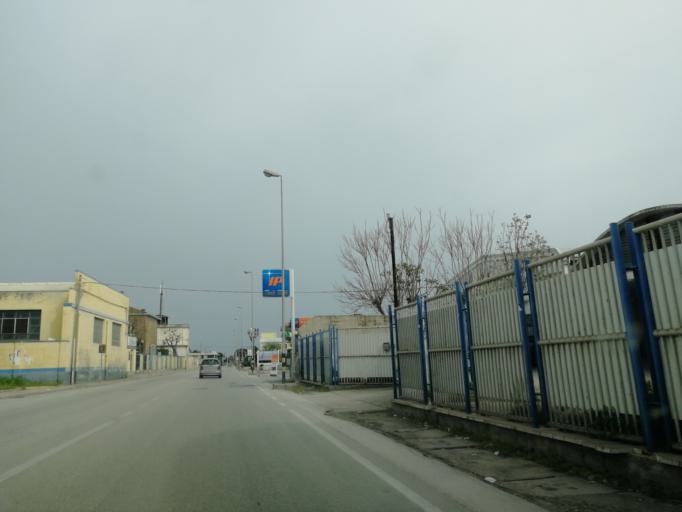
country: IT
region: Apulia
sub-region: Provincia di Barletta - Andria - Trani
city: Barletta
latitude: 41.3174
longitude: 16.2941
